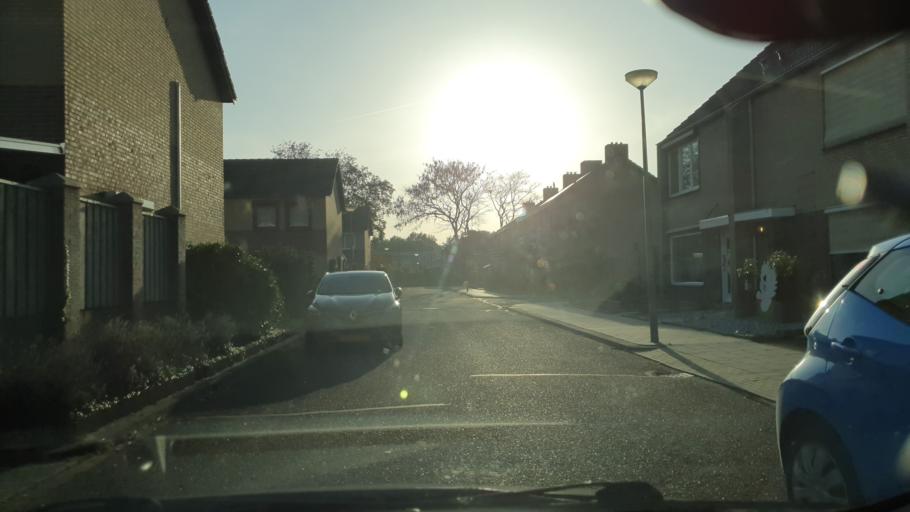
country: NL
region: Limburg
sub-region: Gemeente Roerdalen
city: Sint Odilienberg
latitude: 51.1426
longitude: 5.9966
